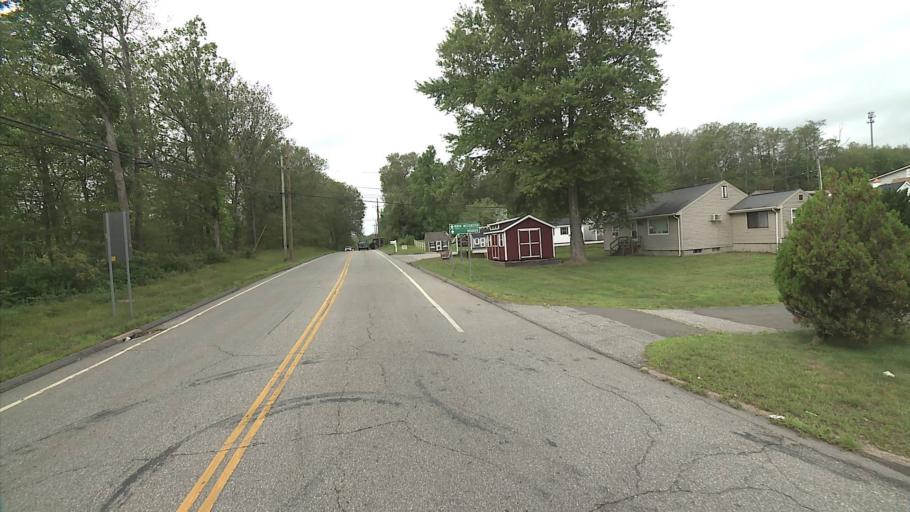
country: US
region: Connecticut
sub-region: New London County
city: Colchester
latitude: 41.5894
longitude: -72.3962
